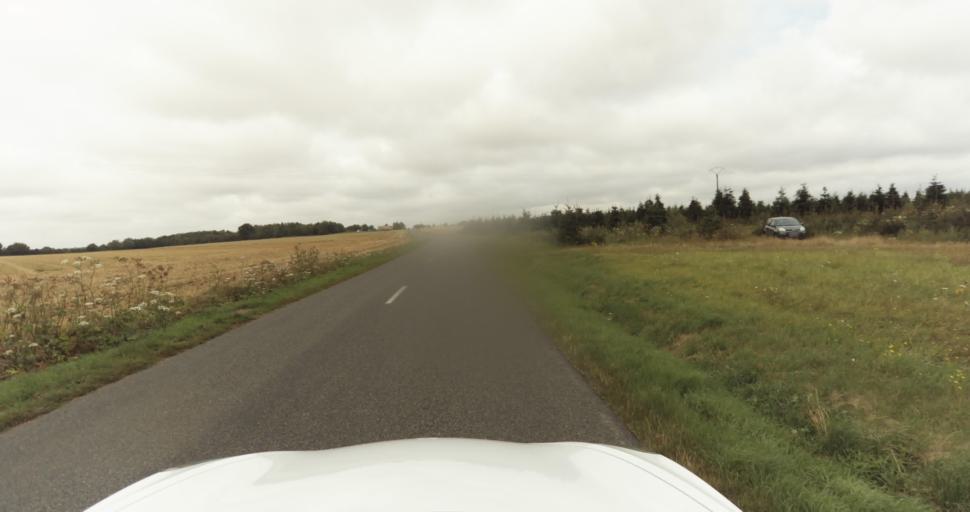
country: FR
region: Haute-Normandie
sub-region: Departement de l'Eure
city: Aviron
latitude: 49.0597
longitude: 1.0802
